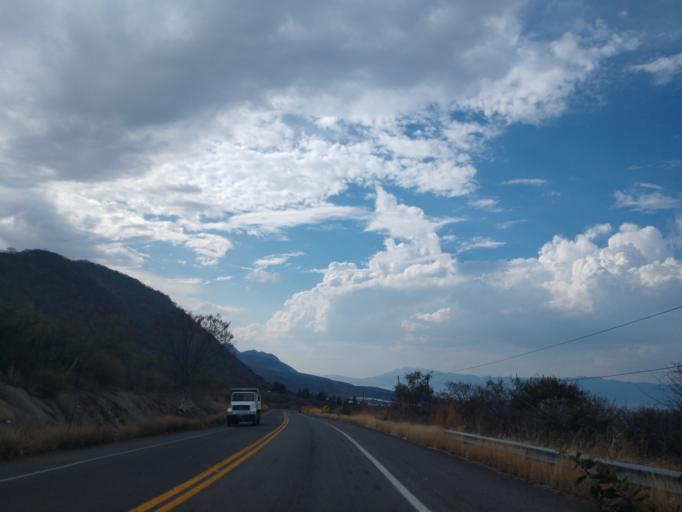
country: MX
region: Jalisco
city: Tizapan el Alto
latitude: 20.1289
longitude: -103.1637
